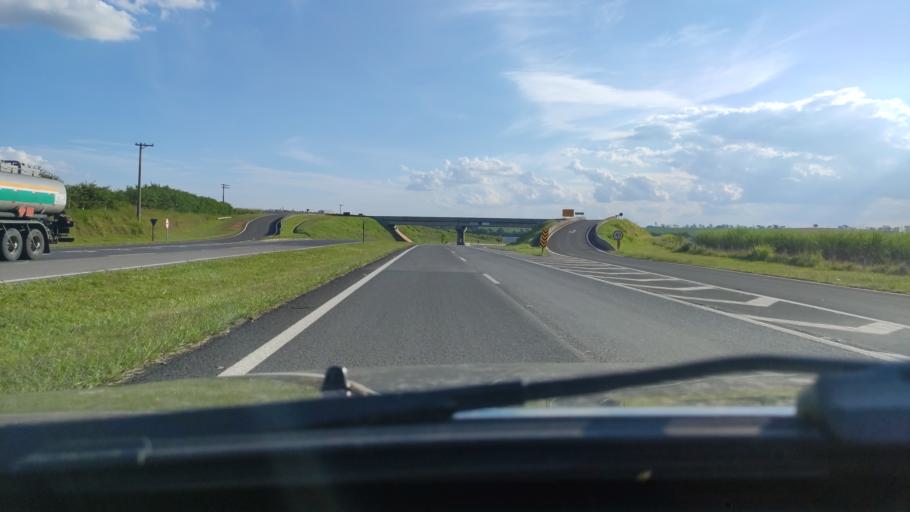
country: BR
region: Sao Paulo
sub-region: Mogi-Mirim
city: Mogi Mirim
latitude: -22.4548
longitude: -46.8949
